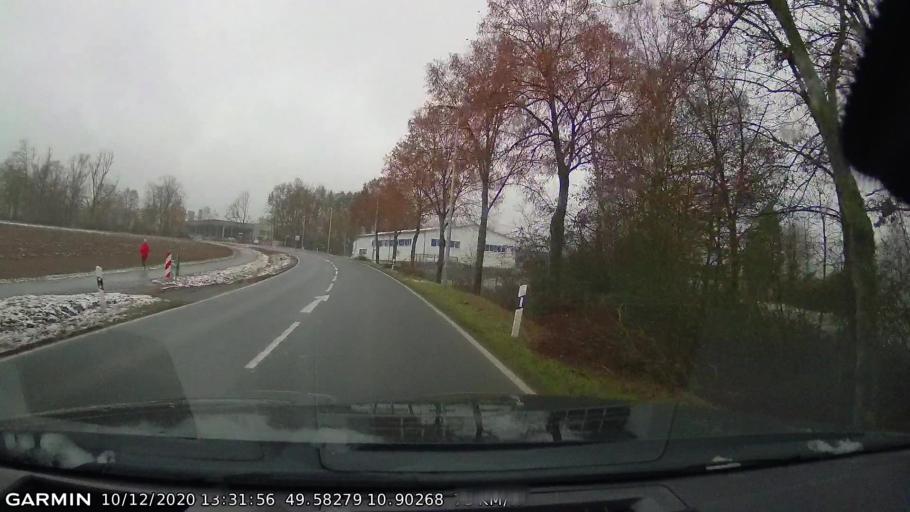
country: DE
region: Bavaria
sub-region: Regierungsbezirk Mittelfranken
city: Herzogenaurach
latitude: 49.5828
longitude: 10.9026
